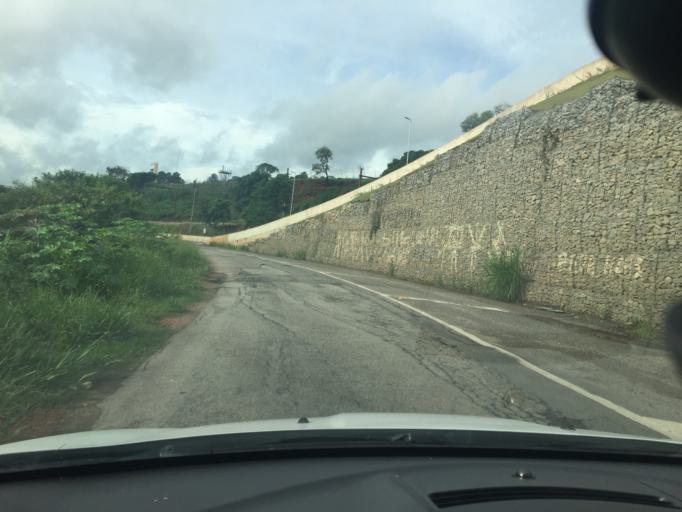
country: BR
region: Sao Paulo
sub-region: Varzea Paulista
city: Varzea Paulista
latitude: -23.2044
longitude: -46.8122
